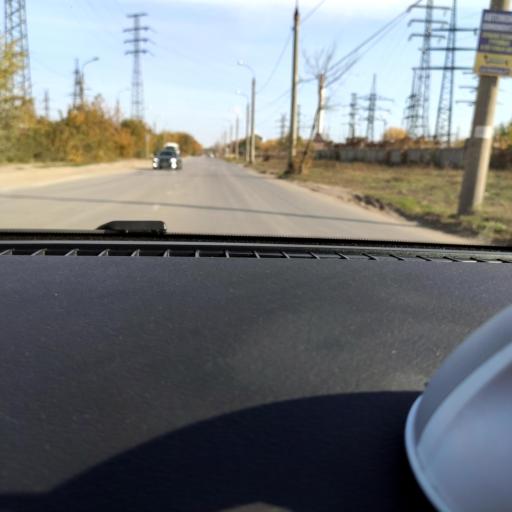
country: RU
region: Samara
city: Smyshlyayevka
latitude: 53.2003
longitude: 50.2891
